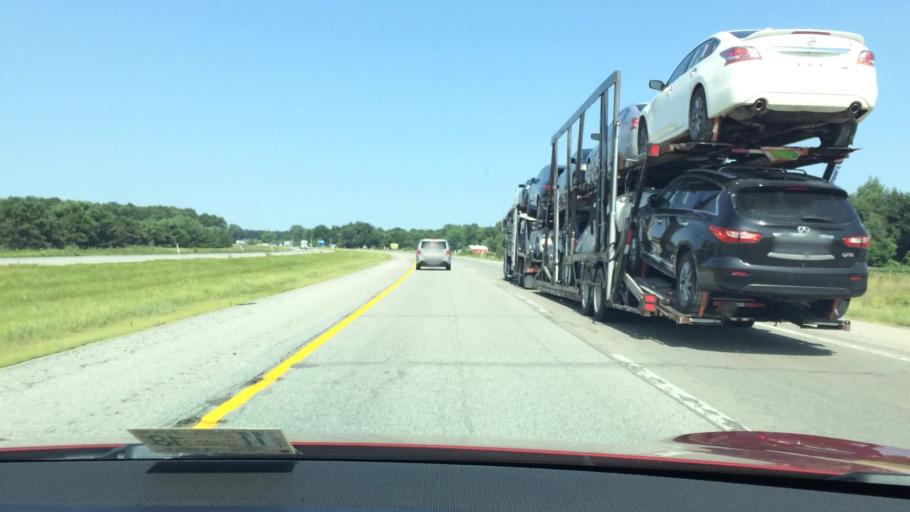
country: US
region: Michigan
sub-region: Saint Joseph County
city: White Pigeon
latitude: 41.7537
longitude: -85.6384
